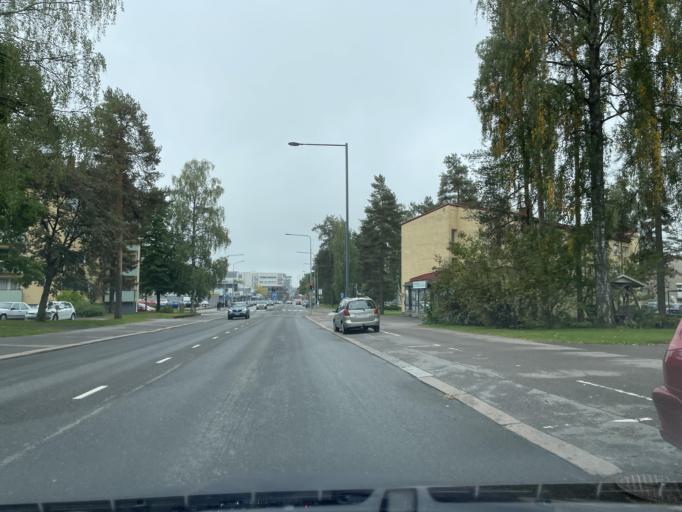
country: FI
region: Uusimaa
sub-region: Helsinki
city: Hyvinge
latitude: 60.6344
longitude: 24.8568
